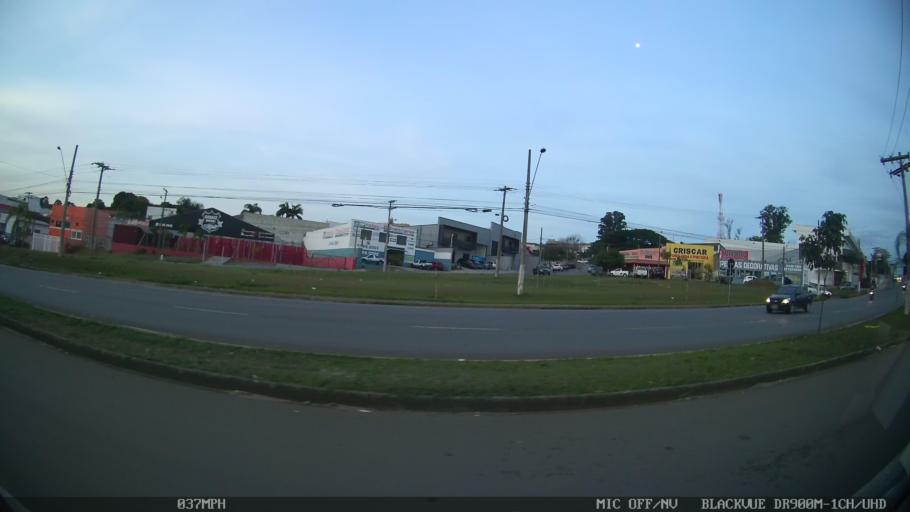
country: BR
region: Sao Paulo
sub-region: Limeira
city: Limeira
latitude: -22.5499
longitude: -47.3839
